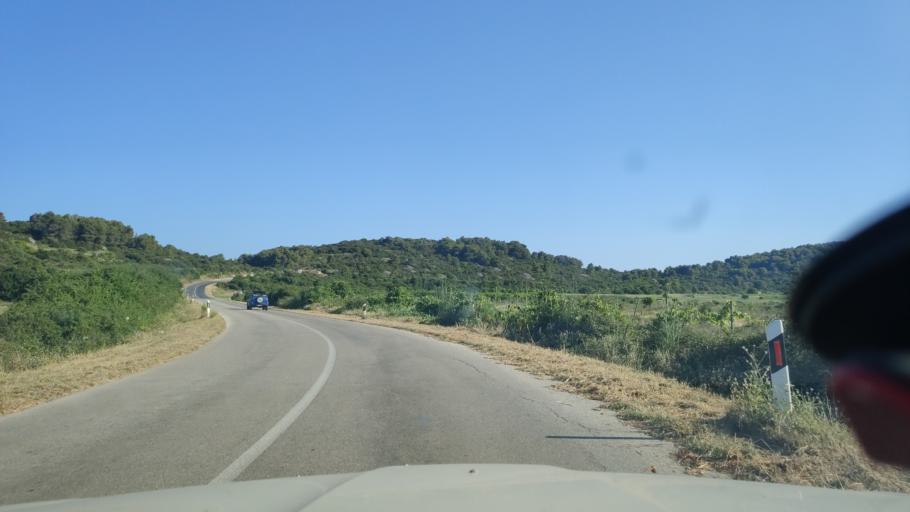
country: HR
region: Splitsko-Dalmatinska
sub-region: Grad Vis
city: Vis
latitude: 43.0415
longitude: 16.1993
